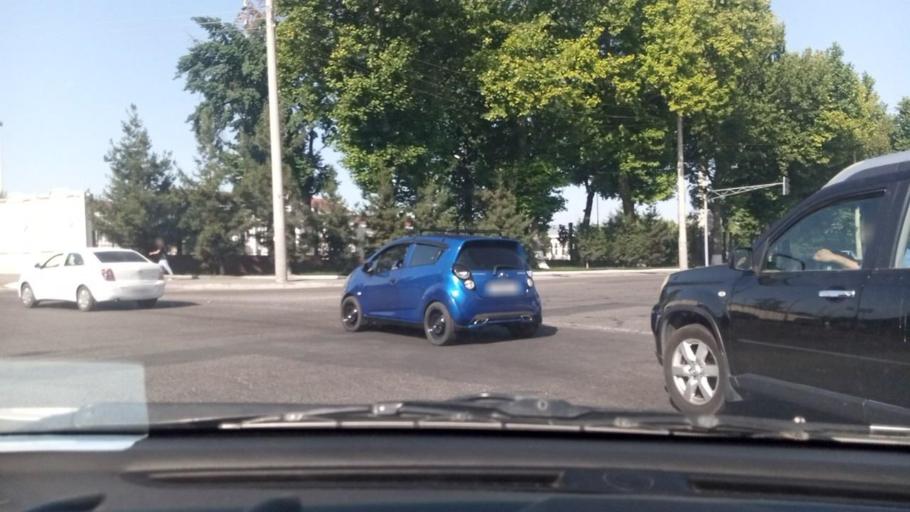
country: UZ
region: Toshkent
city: Salor
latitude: 41.3190
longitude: 69.3111
